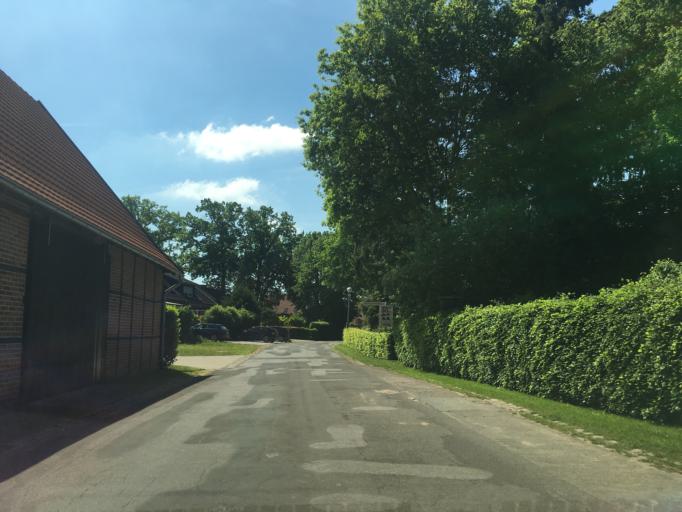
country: DE
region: North Rhine-Westphalia
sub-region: Regierungsbezirk Munster
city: Greven
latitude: 52.0607
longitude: 7.6387
